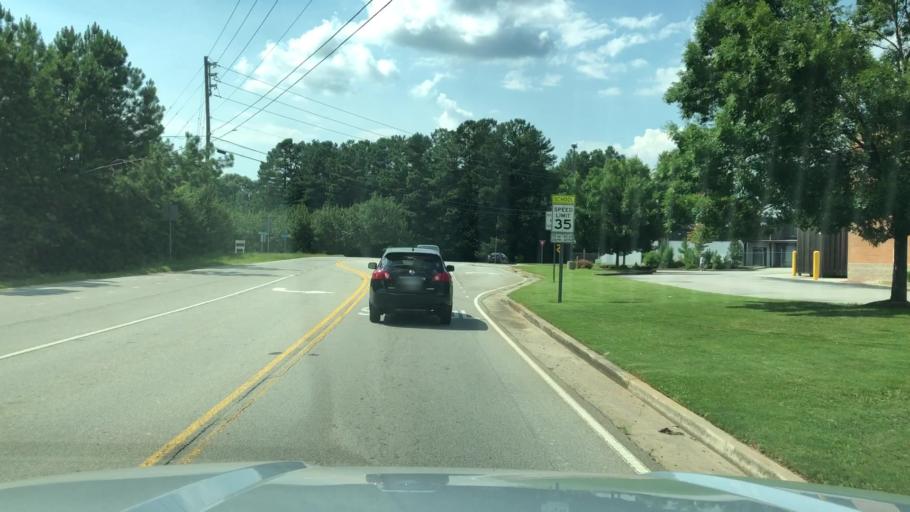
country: US
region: Georgia
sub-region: Paulding County
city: Dallas
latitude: 33.9590
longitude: -84.7894
